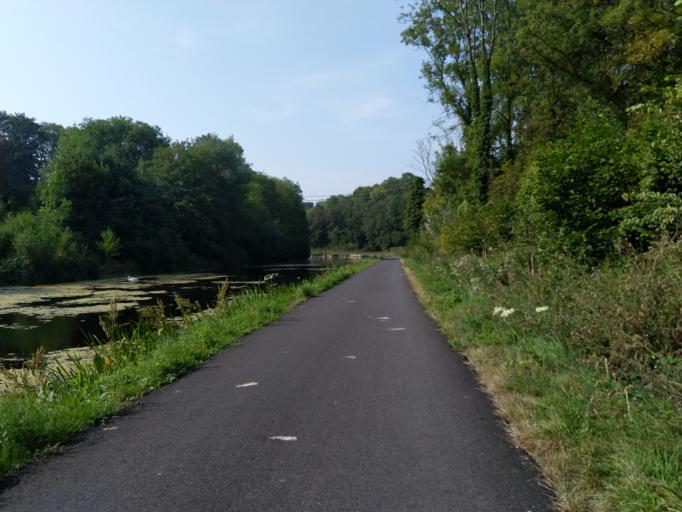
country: BE
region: Wallonia
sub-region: Province du Hainaut
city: Seneffe
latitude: 50.5836
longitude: 4.2529
